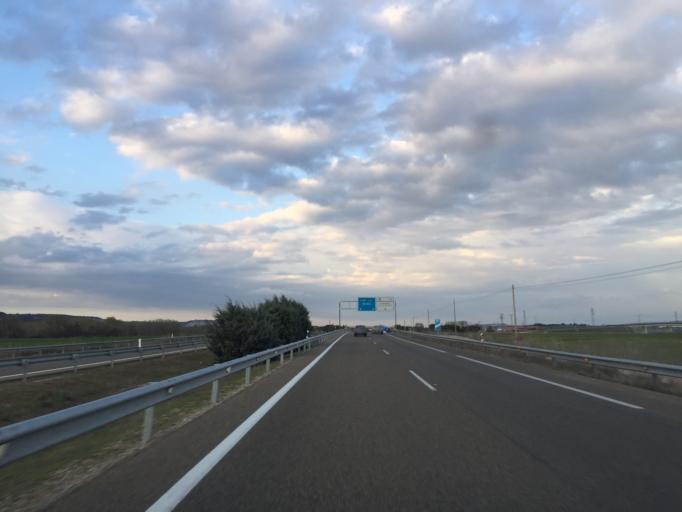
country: ES
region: Castille and Leon
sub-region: Provincia de Palencia
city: Quintana del Puente
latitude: 42.0642
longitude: -4.2293
